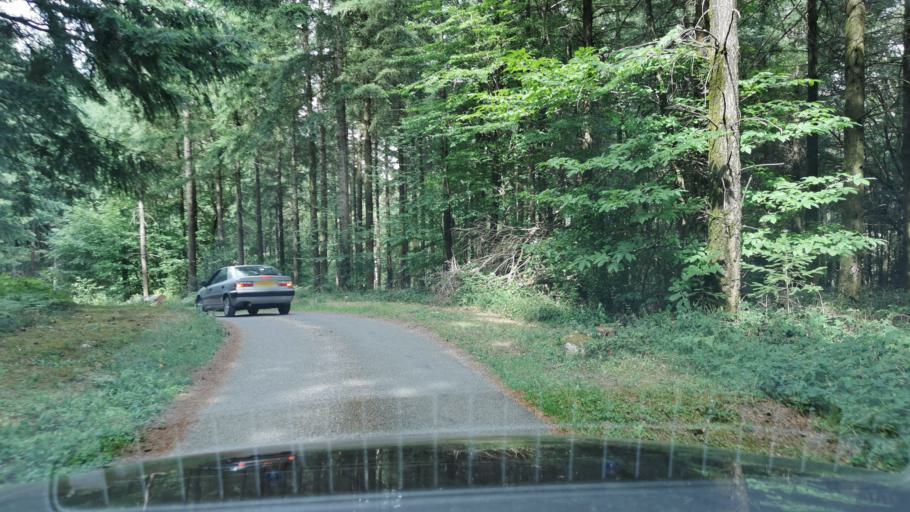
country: FR
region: Bourgogne
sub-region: Departement de Saone-et-Loire
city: Marmagne
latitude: 46.8053
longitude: 4.2765
